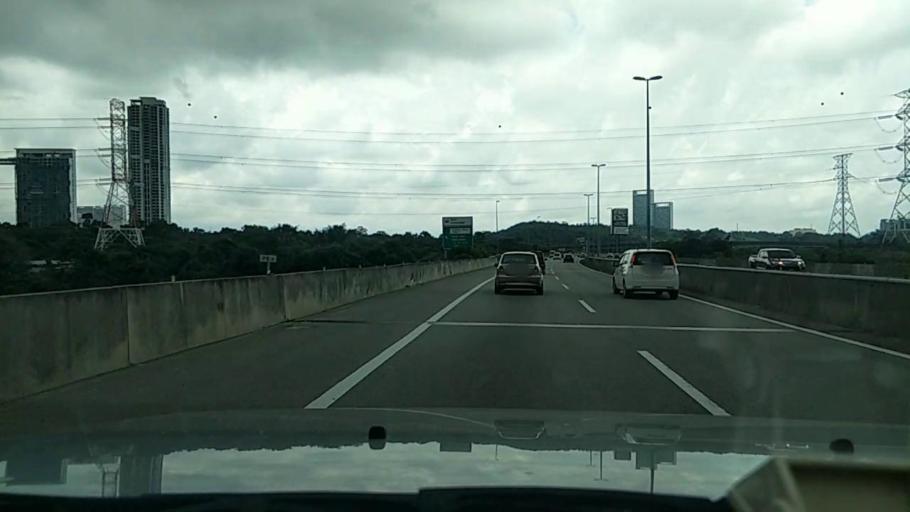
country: MY
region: Putrajaya
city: Putrajaya
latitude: 2.9463
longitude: 101.6468
